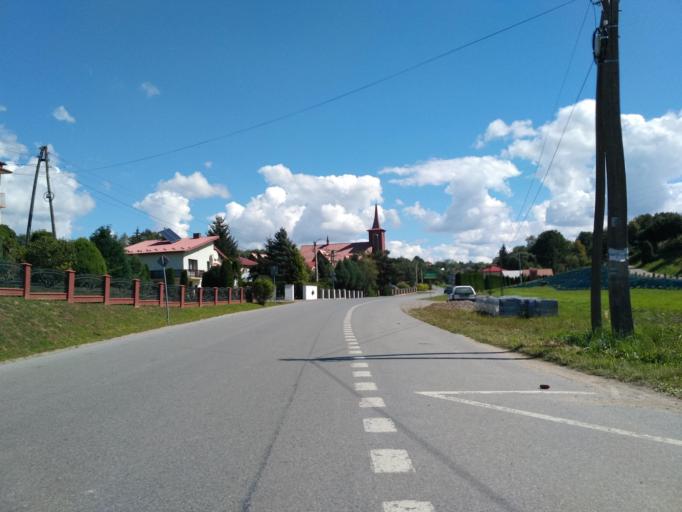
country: PL
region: Subcarpathian Voivodeship
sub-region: Powiat jasielski
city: Skolyszyn
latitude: 49.7914
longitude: 21.3319
